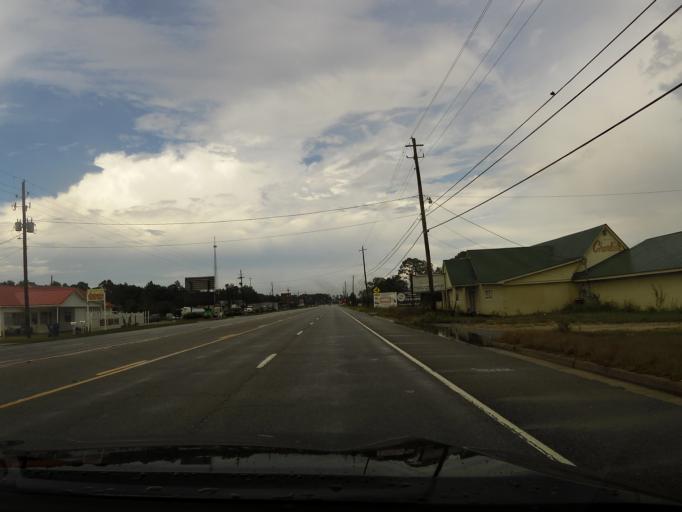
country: US
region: Georgia
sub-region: Wayne County
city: Jesup
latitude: 31.6542
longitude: -81.8522
